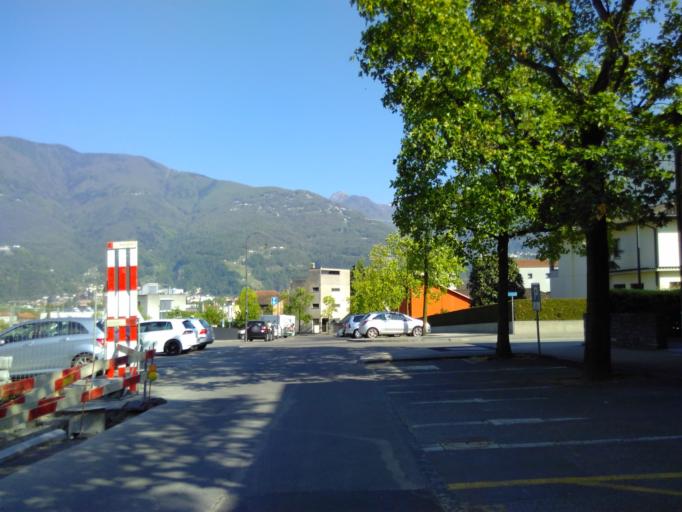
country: CH
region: Ticino
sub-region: Bellinzona District
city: Monte Carasso
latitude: 46.1868
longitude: 8.9968
